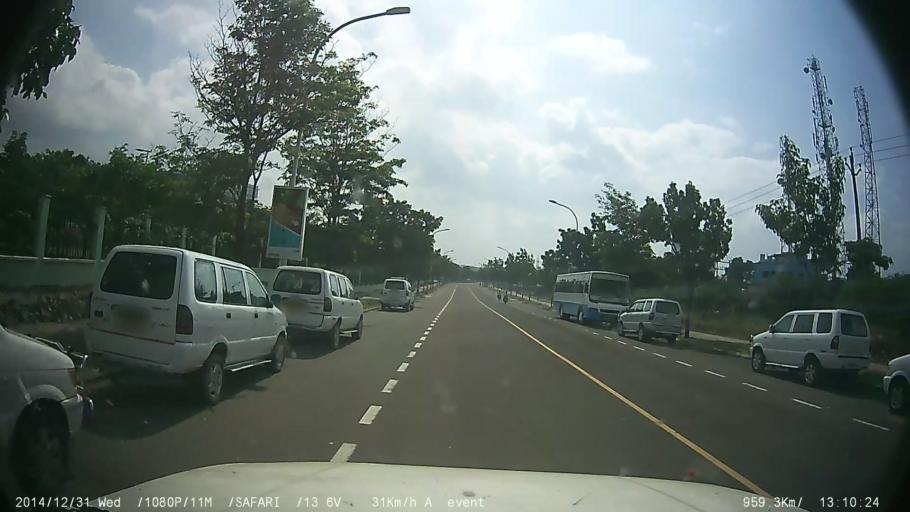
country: IN
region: Tamil Nadu
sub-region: Kancheepuram
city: Singapperumalkovil
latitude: 12.7373
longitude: 80.0029
